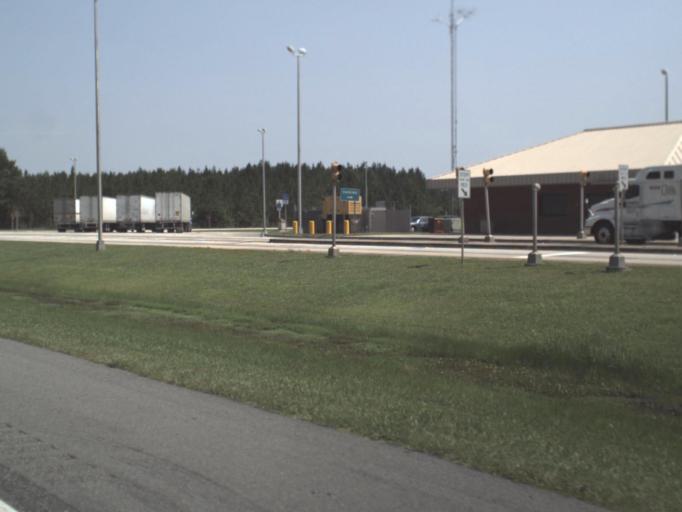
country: US
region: Florida
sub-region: Hamilton County
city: Jasper
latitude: 30.4176
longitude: -82.8987
